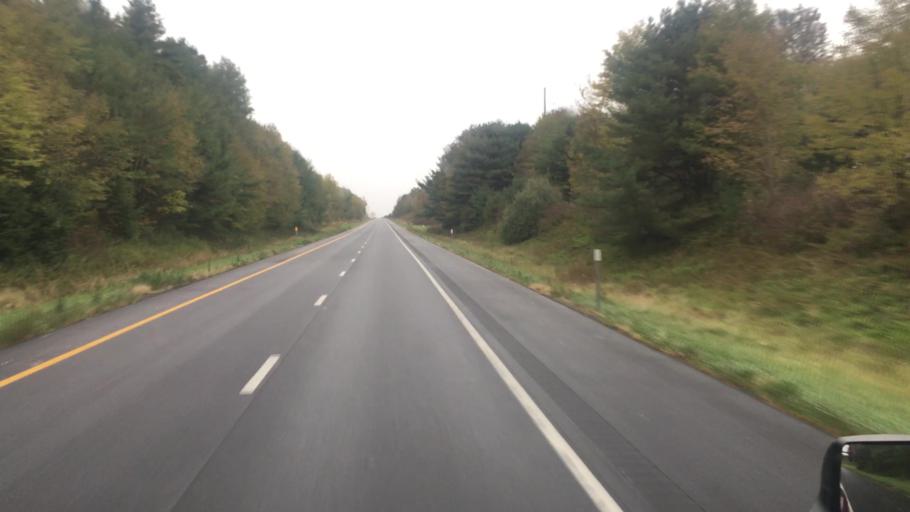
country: US
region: New York
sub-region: Chenango County
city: Bainbridge
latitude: 42.1981
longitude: -75.5481
